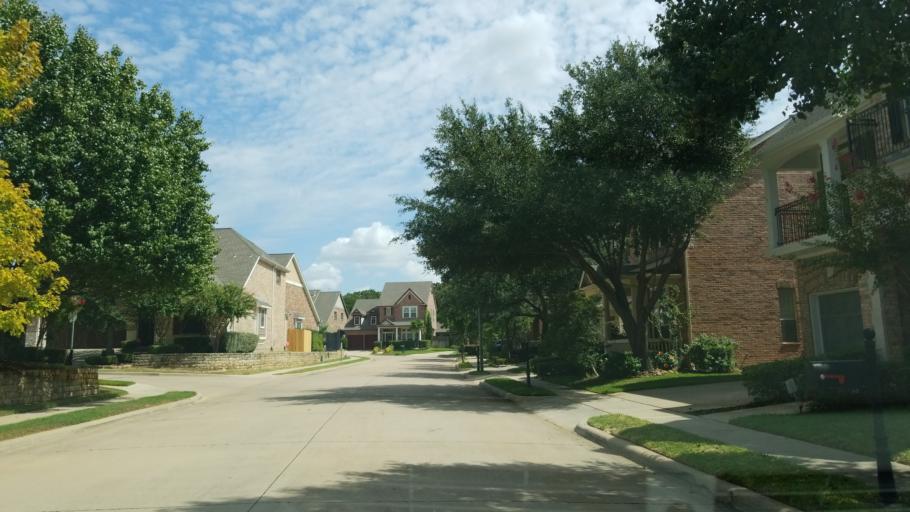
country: US
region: Texas
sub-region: Tarrant County
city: Euless
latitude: 32.8689
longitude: -97.0930
